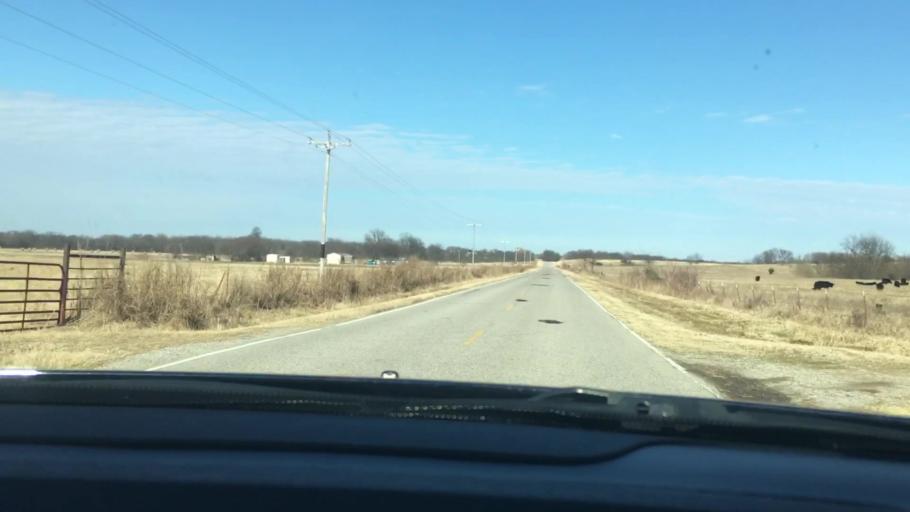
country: US
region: Oklahoma
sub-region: Garvin County
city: Wynnewood
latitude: 34.7131
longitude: -97.1254
